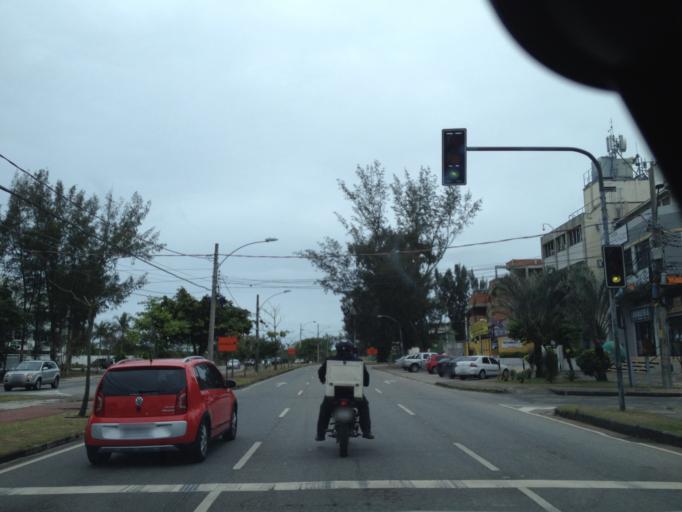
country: BR
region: Rio de Janeiro
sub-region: Nilopolis
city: Nilopolis
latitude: -23.0112
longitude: -43.4428
